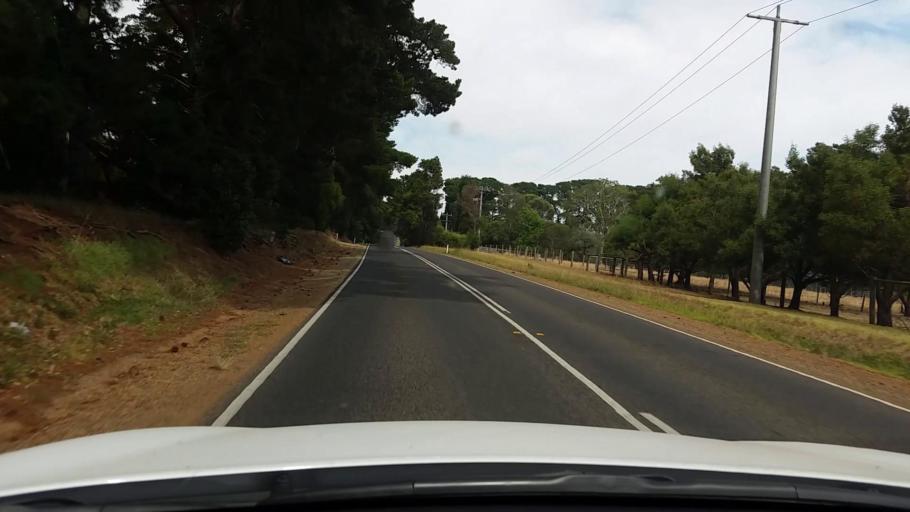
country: AU
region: Victoria
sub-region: Mornington Peninsula
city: Merricks
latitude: -38.3872
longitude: 145.0967
